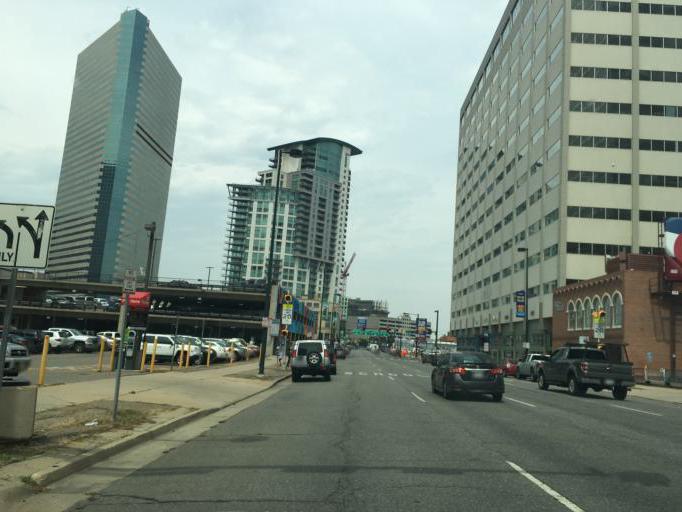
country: US
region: Colorado
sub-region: Denver County
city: Denver
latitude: 39.7449
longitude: -104.9862
